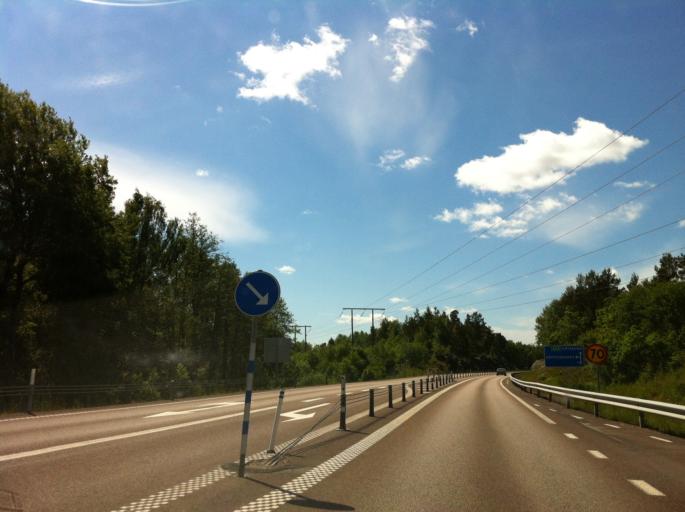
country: SE
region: Vaestra Goetaland
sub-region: Melleruds Kommun
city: Mellerud
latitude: 58.7846
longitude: 12.5129
